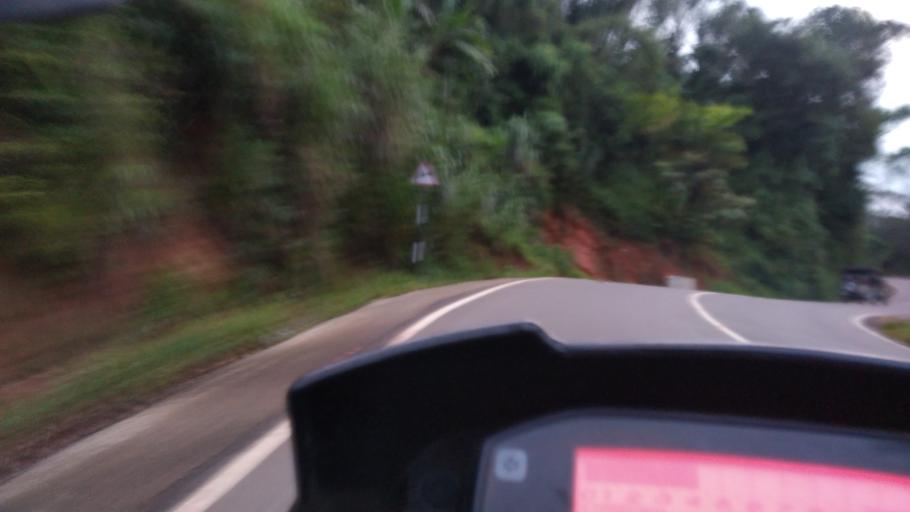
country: IN
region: Kerala
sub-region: Idukki
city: Munnar
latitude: 9.9695
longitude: 77.1221
